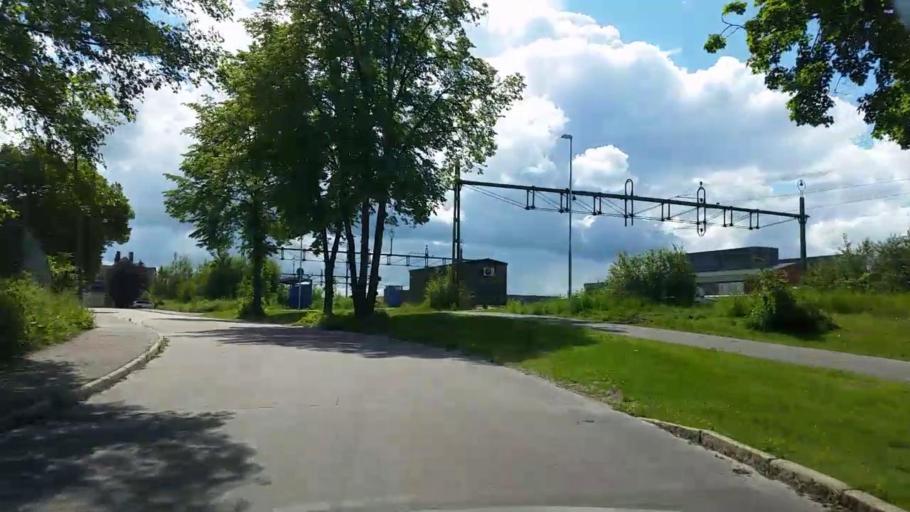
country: SE
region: Vaestmanland
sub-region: Fagersta Kommun
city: Fagersta
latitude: 60.0035
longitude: 15.7866
